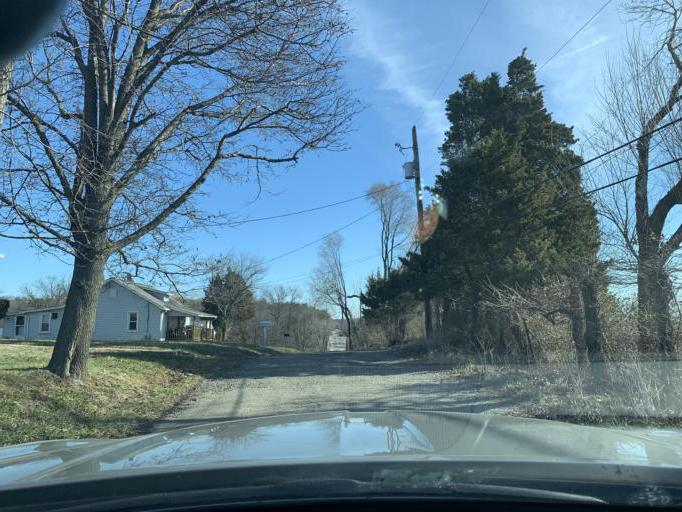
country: US
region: Maryland
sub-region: Prince George's County
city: Beltsville
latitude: 39.0652
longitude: -76.8955
